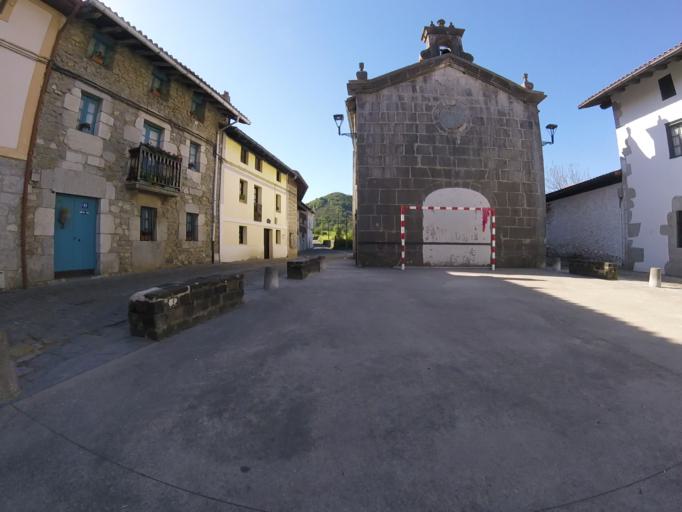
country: ES
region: Basque Country
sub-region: Provincia de Guipuzcoa
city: Aizarnazabal
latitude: 43.2343
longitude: -2.2252
